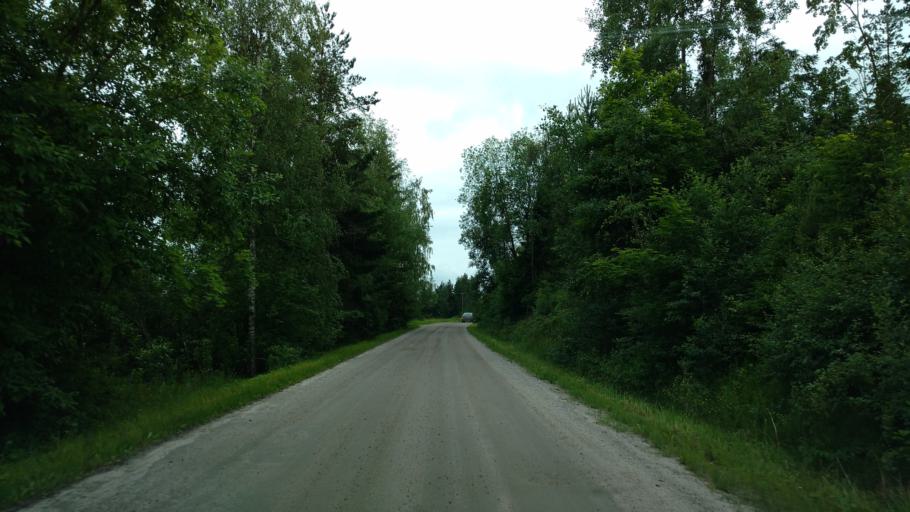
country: FI
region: Varsinais-Suomi
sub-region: Salo
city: Halikko
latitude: 60.4736
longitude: 23.0021
